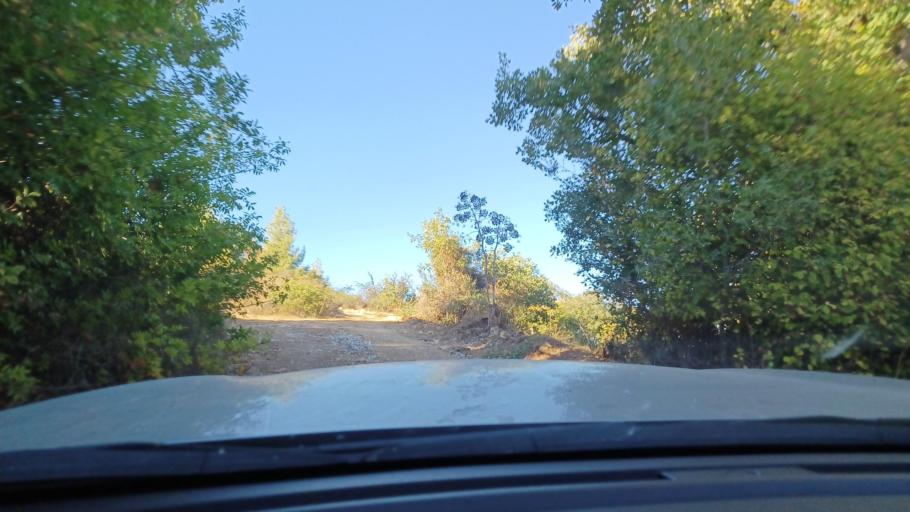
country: CY
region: Pafos
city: Polis
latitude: 34.9962
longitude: 32.5055
